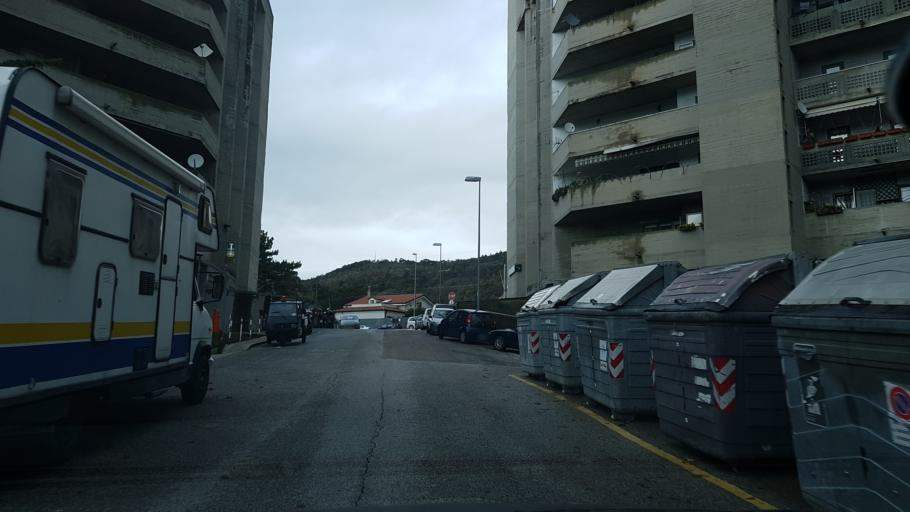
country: IT
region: Friuli Venezia Giulia
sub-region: Provincia di Trieste
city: Domio
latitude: 45.6403
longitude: 13.8252
